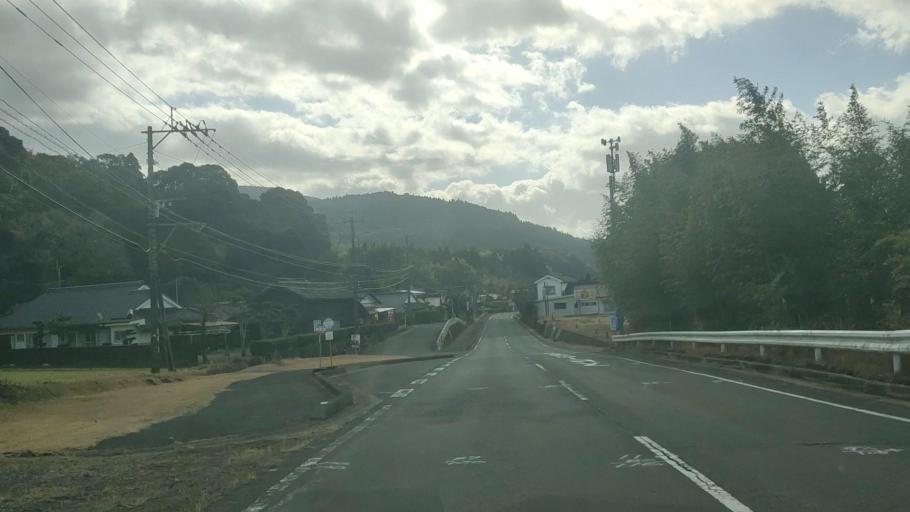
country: JP
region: Kagoshima
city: Okuchi-shinohara
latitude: 31.9937
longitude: 130.7483
